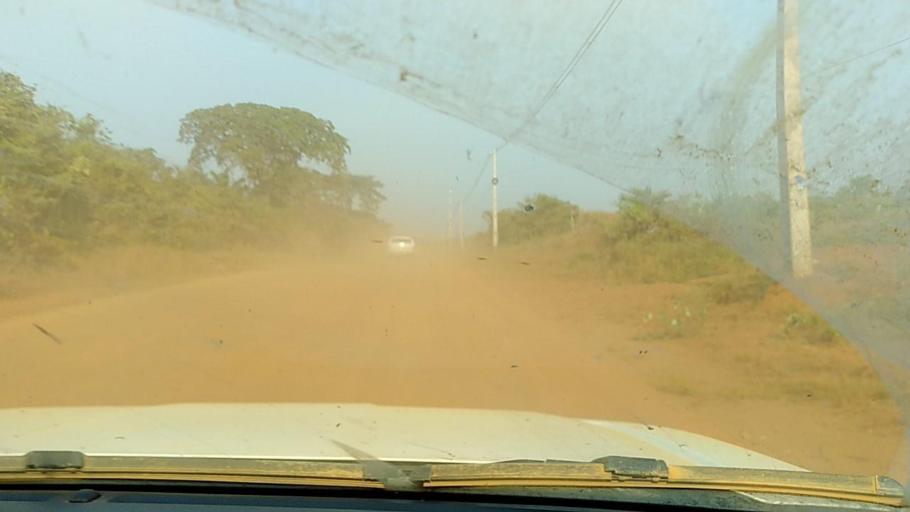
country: BR
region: Rondonia
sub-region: Porto Velho
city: Porto Velho
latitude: -8.7585
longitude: -63.9647
